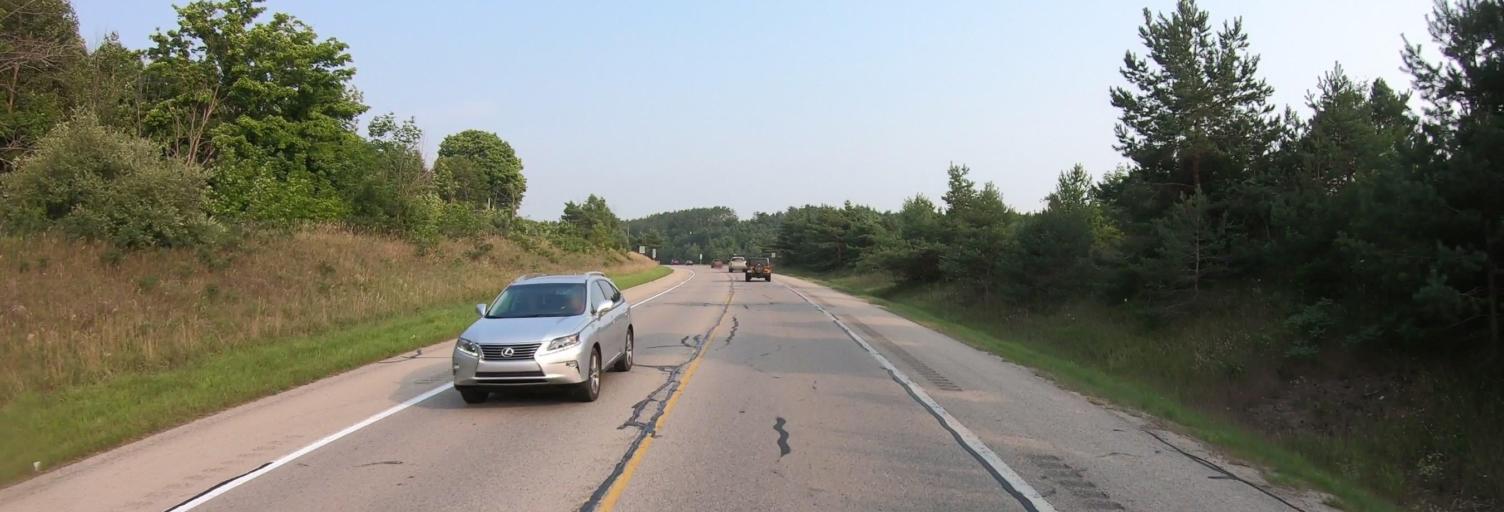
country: US
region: Michigan
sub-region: Emmet County
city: Harbor Springs
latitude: 45.3637
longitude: -85.1160
